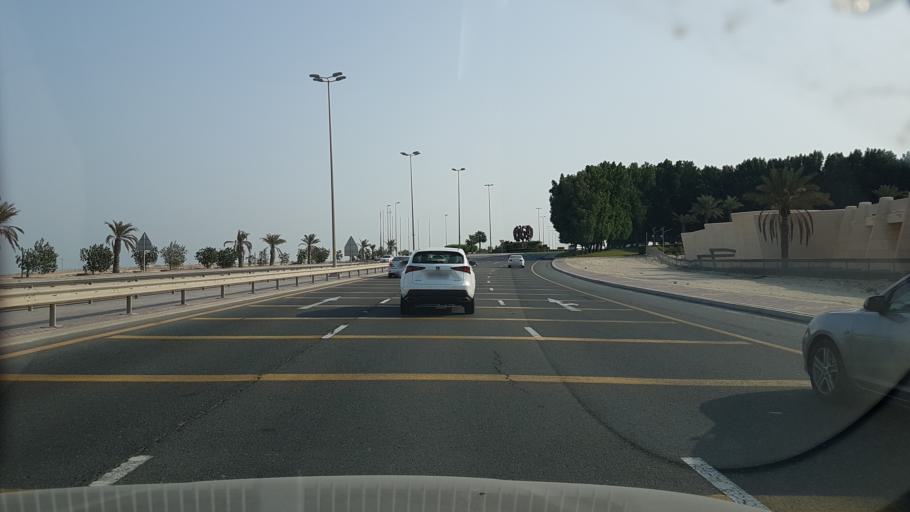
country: BH
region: Central Governorate
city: Dar Kulayb
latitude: 26.0720
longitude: 50.5258
